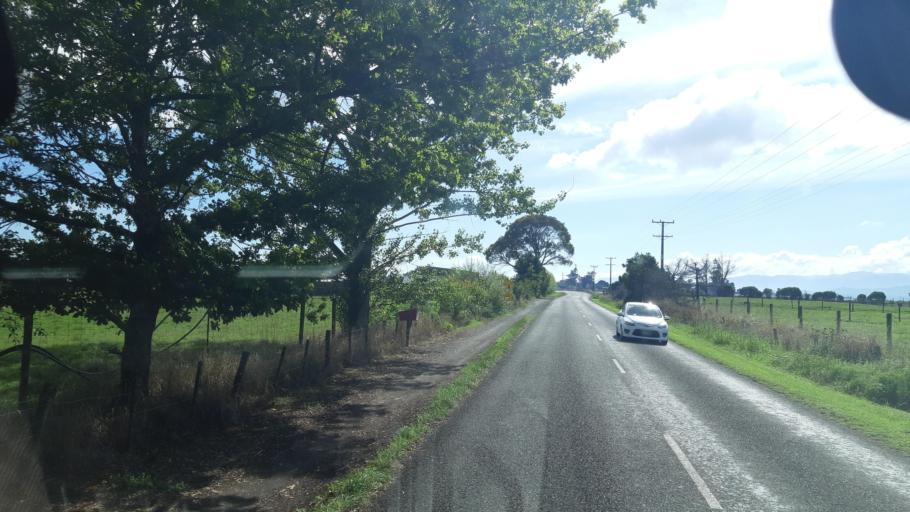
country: NZ
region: Tasman
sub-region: Tasman District
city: Richmond
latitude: -41.3058
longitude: 173.1522
